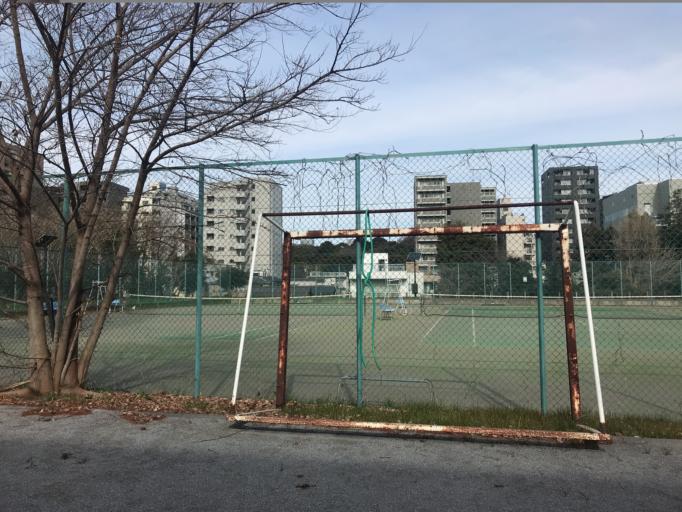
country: JP
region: Tokyo
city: Tokyo
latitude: 35.7193
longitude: 139.7296
